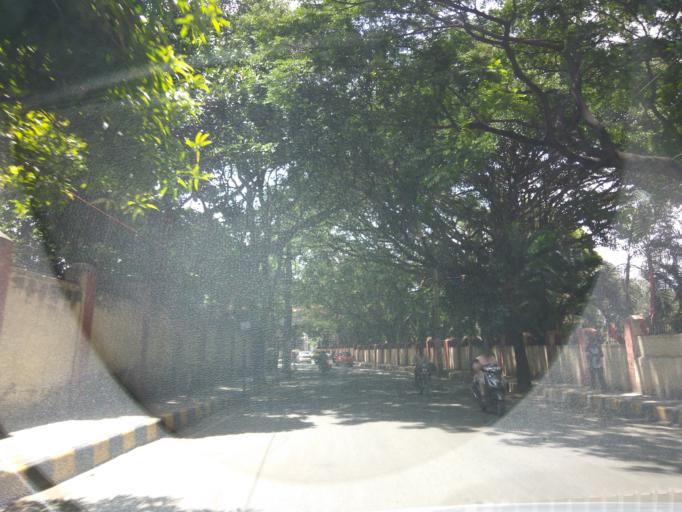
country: IN
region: Karnataka
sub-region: Bangalore Urban
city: Bangalore
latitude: 12.9866
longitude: 77.6639
